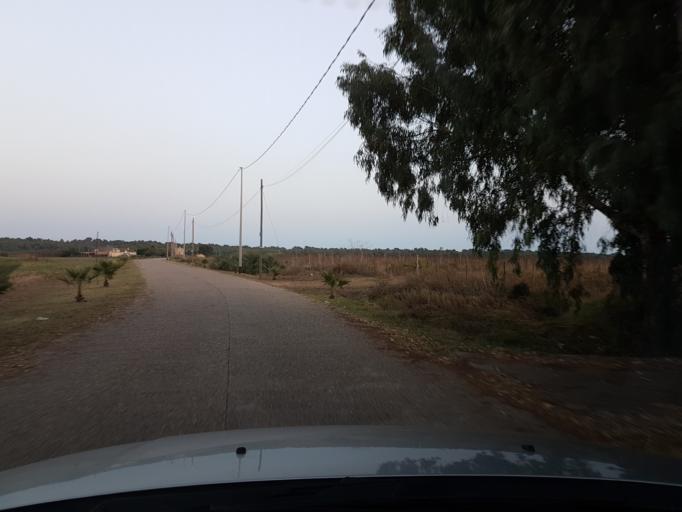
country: IT
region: Sardinia
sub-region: Provincia di Oristano
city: Cabras
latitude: 39.9169
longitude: 8.5079
